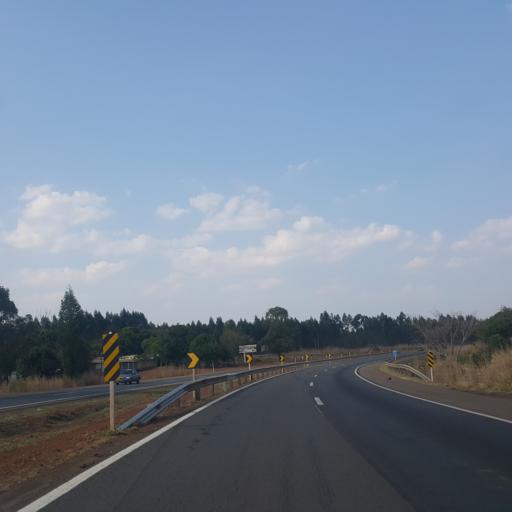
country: BR
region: Goias
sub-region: Abadiania
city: Abadiania
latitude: -16.1852
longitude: -48.6967
